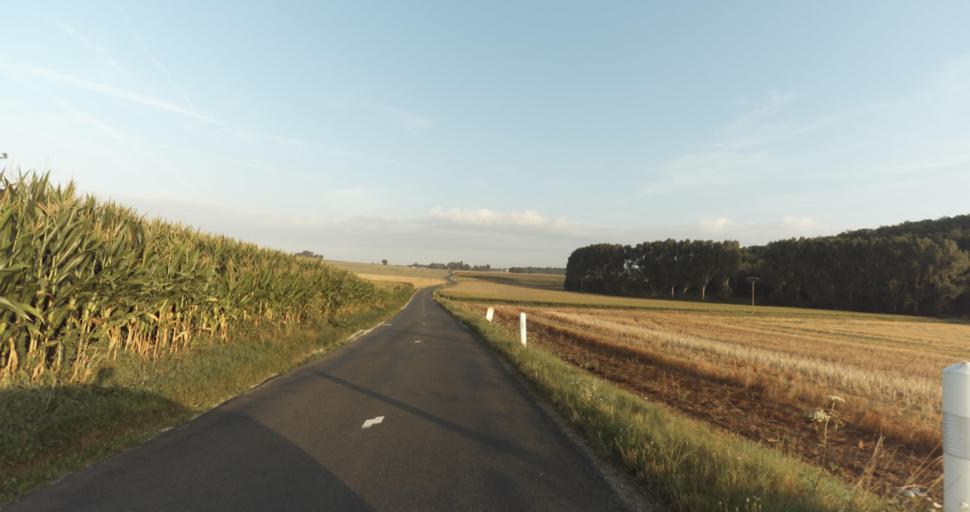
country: FR
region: Haute-Normandie
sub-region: Departement de l'Eure
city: Marcilly-sur-Eure
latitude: 48.7897
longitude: 1.3351
